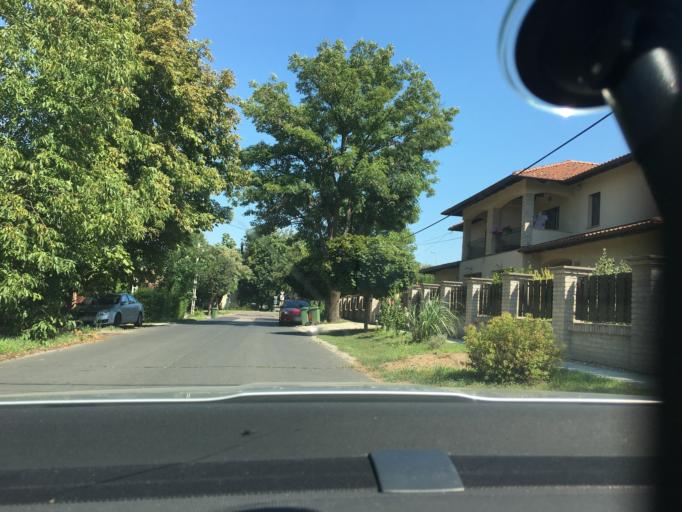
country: HU
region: Budapest
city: Budapest XVI. keruelet
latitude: 47.5031
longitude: 19.1870
